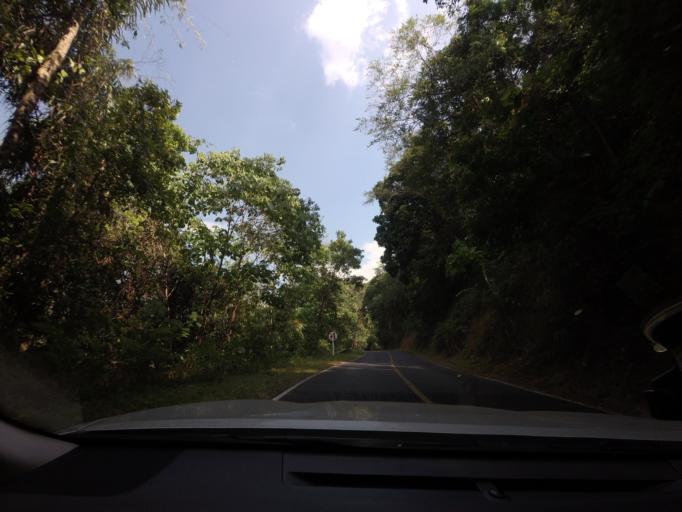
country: TH
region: Phangnga
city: Phang Nga
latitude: 8.5356
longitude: 98.5531
